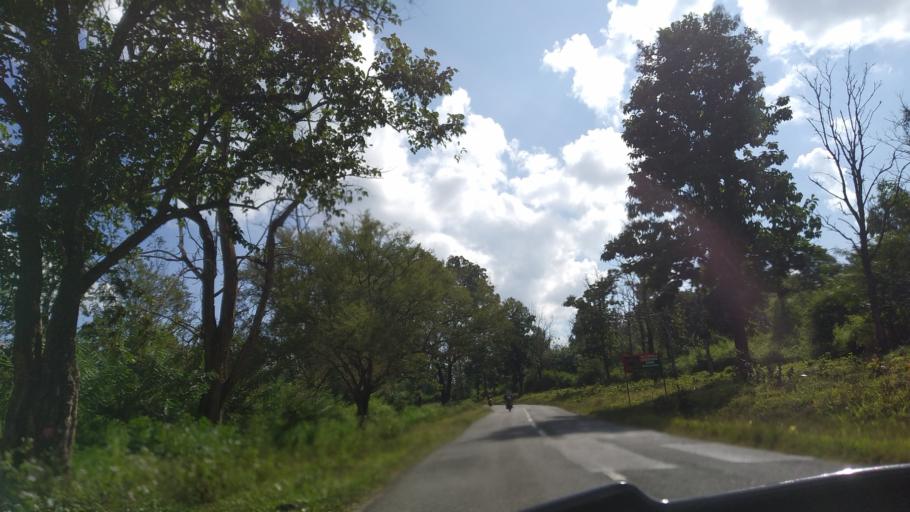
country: IN
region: Kerala
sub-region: Wayanad
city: Panamaram
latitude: 11.9286
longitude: 76.0656
